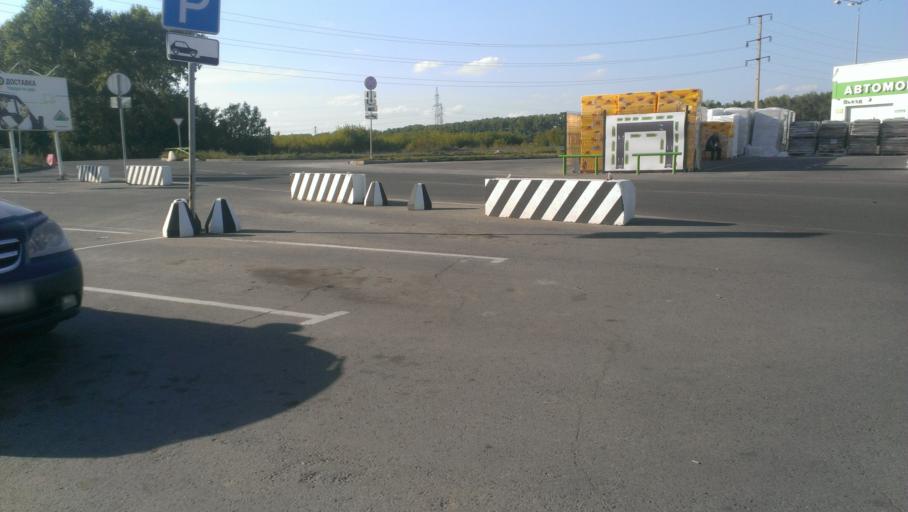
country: RU
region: Altai Krai
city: Novosilikatnyy
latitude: 53.3496
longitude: 83.6307
